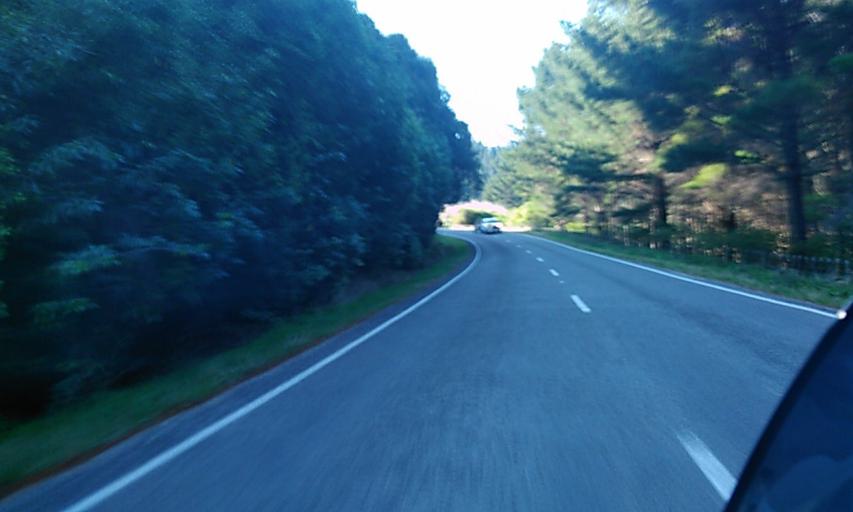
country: NZ
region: Gisborne
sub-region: Gisborne District
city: Gisborne
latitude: -38.5937
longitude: 177.9799
